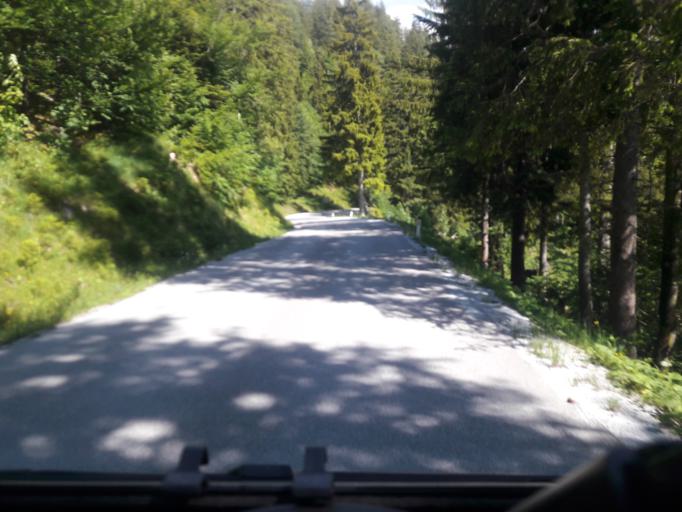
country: AT
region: Styria
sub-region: Politischer Bezirk Liezen
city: Tauplitz
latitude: 47.5819
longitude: 13.9637
